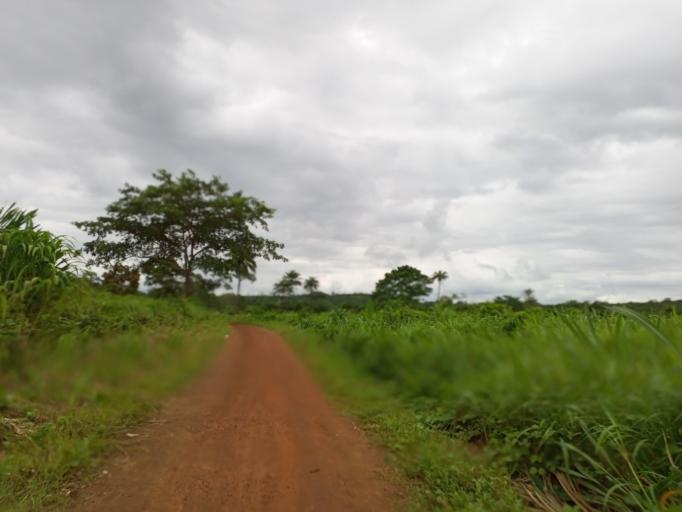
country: SL
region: Northern Province
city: Kamakwie
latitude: 9.5045
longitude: -12.2684
